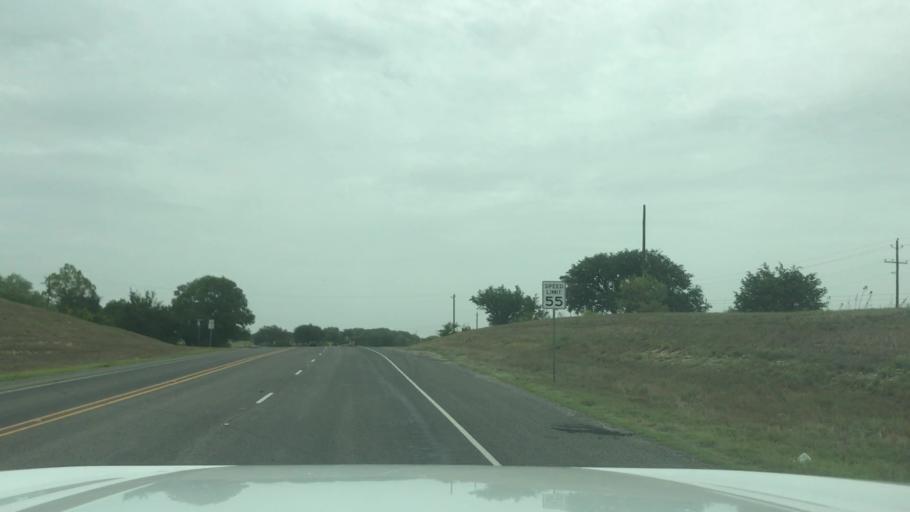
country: US
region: Texas
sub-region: Hamilton County
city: Hico
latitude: 31.9811
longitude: -98.0242
